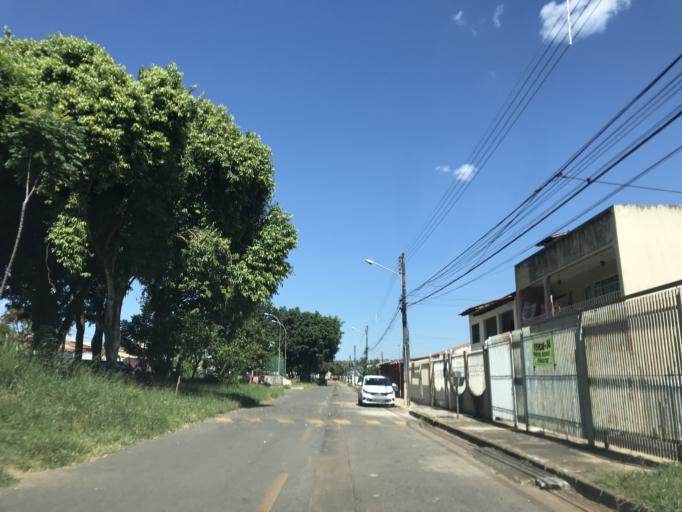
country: BR
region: Federal District
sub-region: Brasilia
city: Brasilia
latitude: -15.6574
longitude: -47.8079
